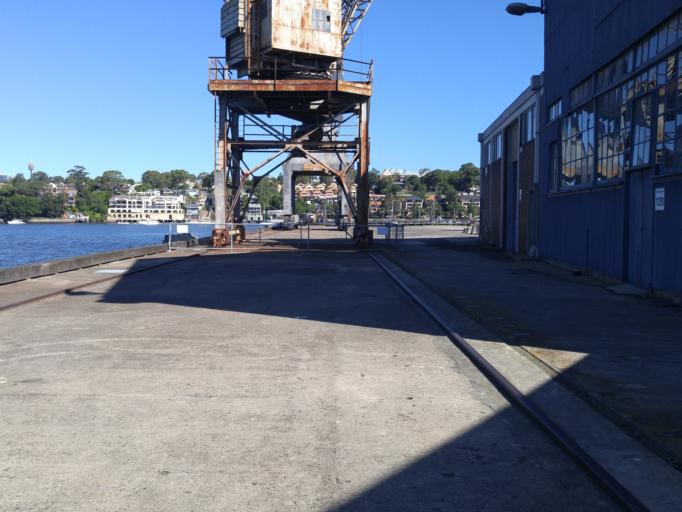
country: AU
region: New South Wales
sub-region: Leichhardt
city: Balmain
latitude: -33.8477
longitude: 151.1746
